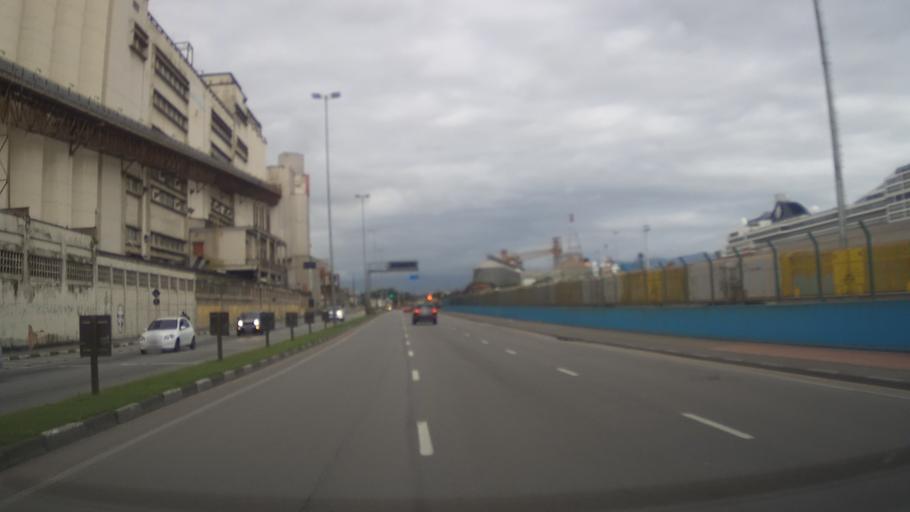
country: BR
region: Sao Paulo
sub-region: Santos
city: Santos
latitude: -23.9605
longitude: -46.3062
